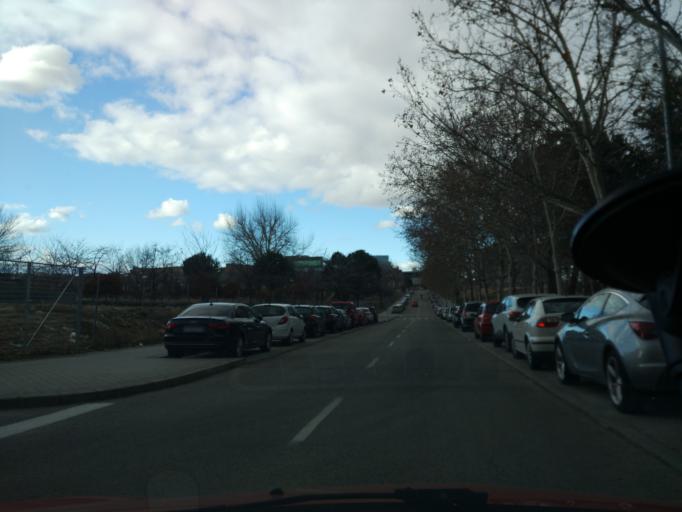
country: ES
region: Madrid
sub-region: Provincia de Madrid
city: San Blas
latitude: 40.4446
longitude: -3.6318
